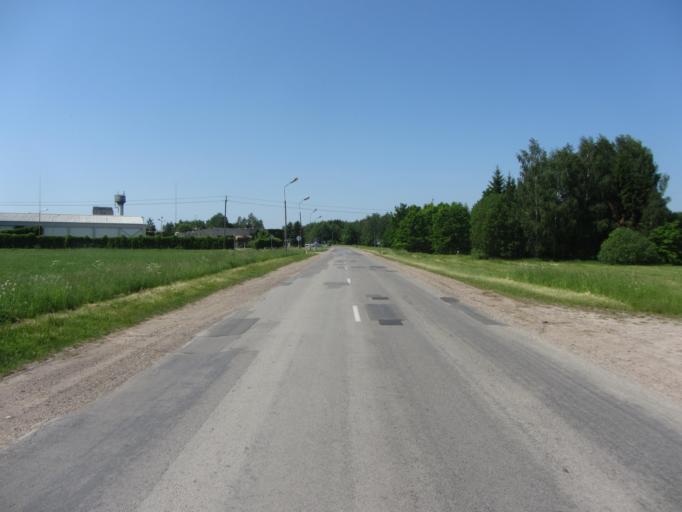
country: LT
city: Kaisiadorys
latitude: 54.8678
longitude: 24.4131
